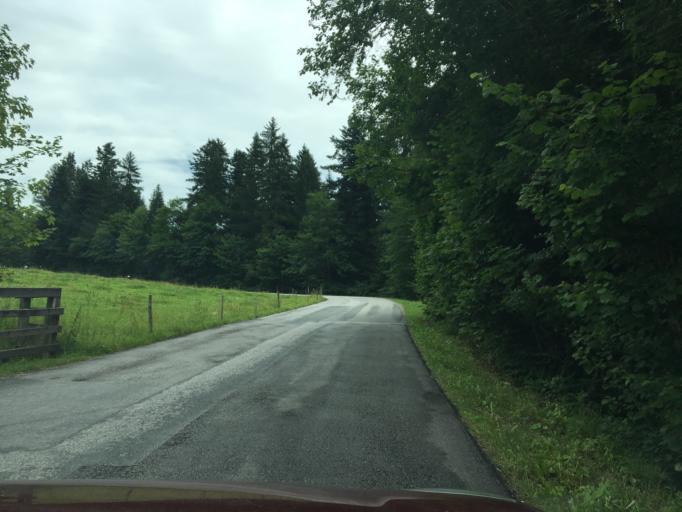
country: AT
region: Salzburg
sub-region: Politischer Bezirk Hallein
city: Abtenau
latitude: 47.5998
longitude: 13.3436
